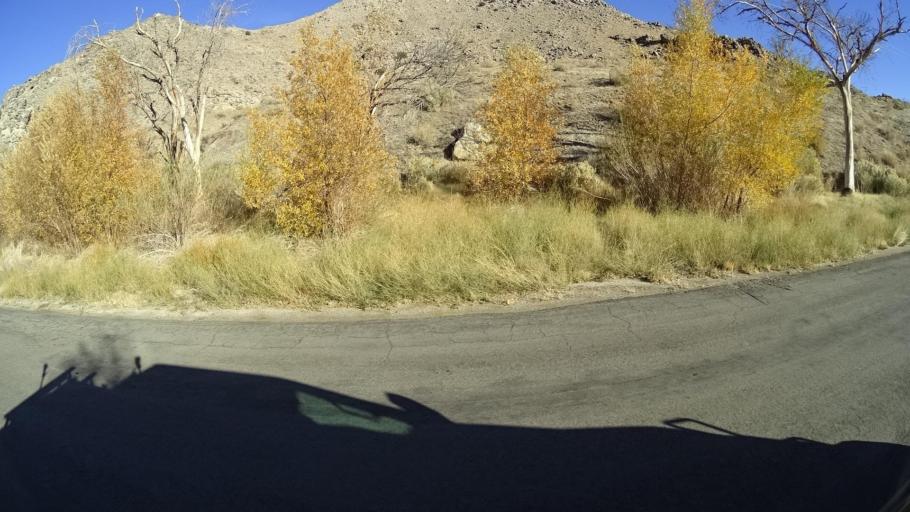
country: US
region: California
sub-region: Kern County
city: Weldon
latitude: 35.5746
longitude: -118.2514
